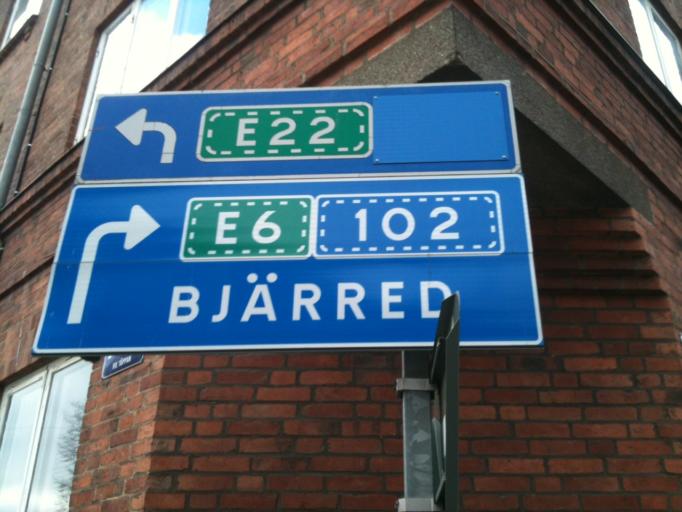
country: SE
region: Skane
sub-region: Lunds Kommun
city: Lund
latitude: 55.6987
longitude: 13.1958
